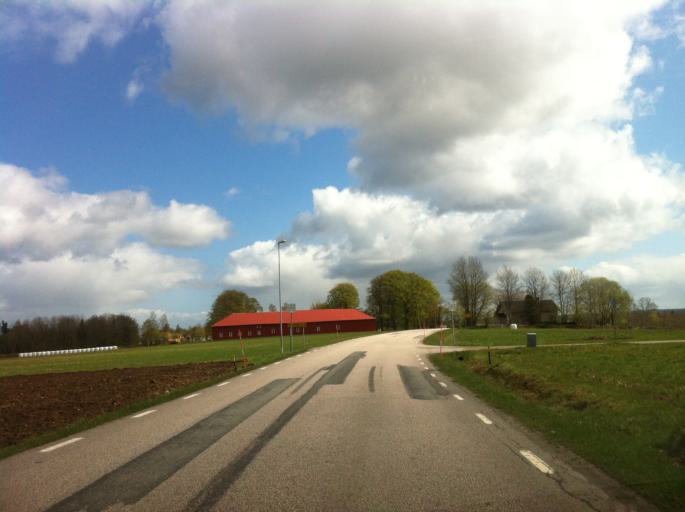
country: SE
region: Vaestra Goetaland
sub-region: Alingsas Kommun
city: Ingared
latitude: 57.8130
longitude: 12.5513
